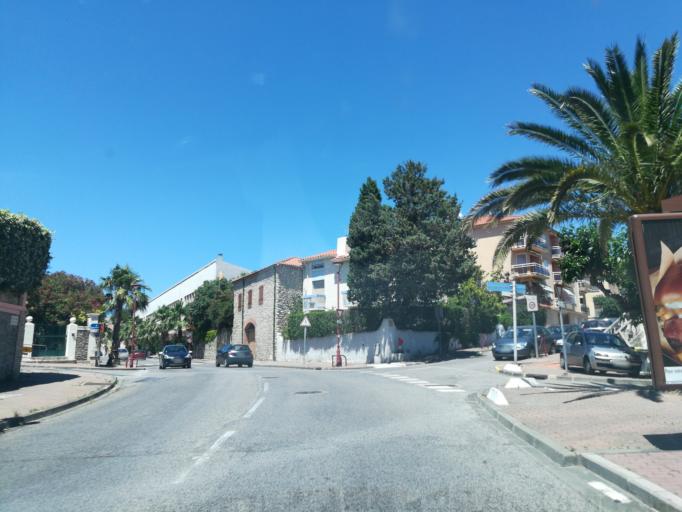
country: FR
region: Languedoc-Roussillon
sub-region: Departement des Pyrenees-Orientales
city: el Volo
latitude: 42.5220
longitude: 2.8323
